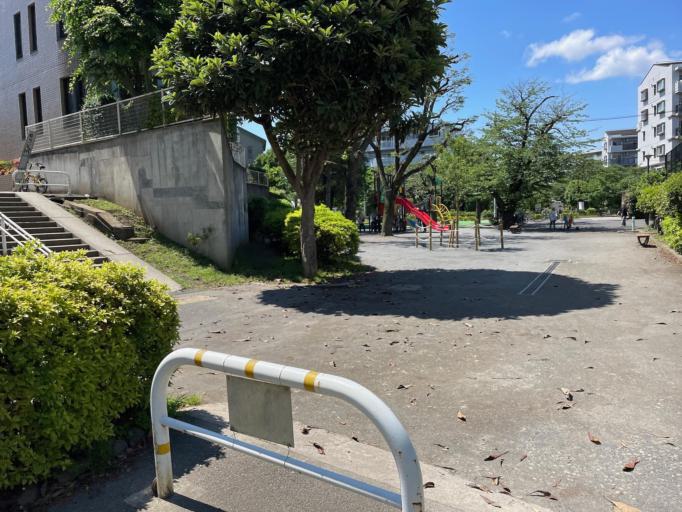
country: JP
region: Tokyo
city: Mitaka-shi
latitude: 35.6546
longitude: 139.6254
